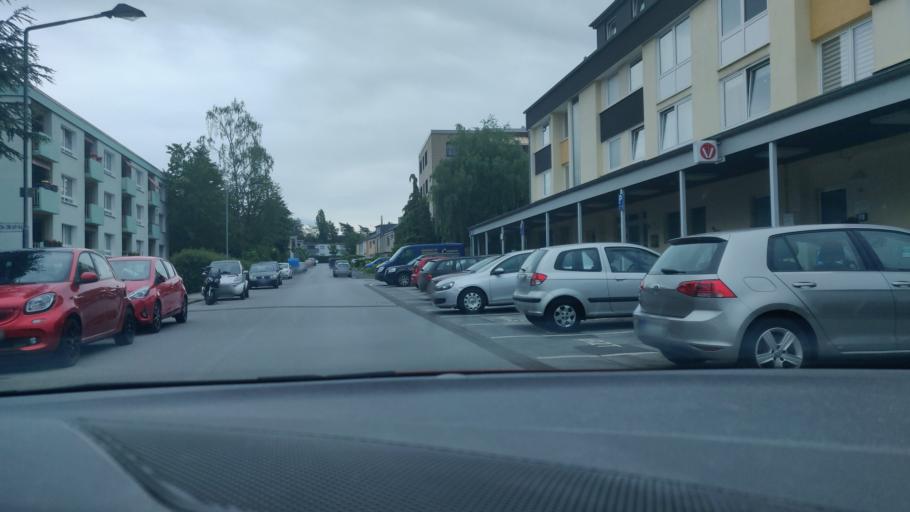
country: DE
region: North Rhine-Westphalia
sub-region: Regierungsbezirk Dusseldorf
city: Heiligenhaus
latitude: 51.2985
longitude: 6.9242
